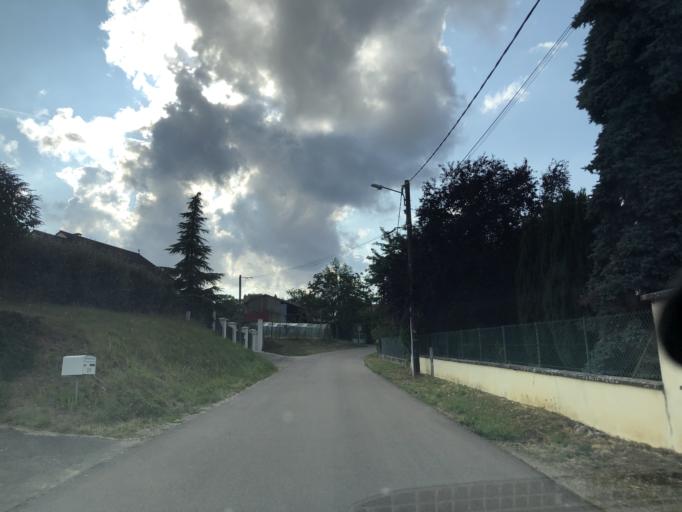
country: FR
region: Bourgogne
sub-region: Departement de l'Yonne
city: Charbuy
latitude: 47.8255
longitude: 3.4577
